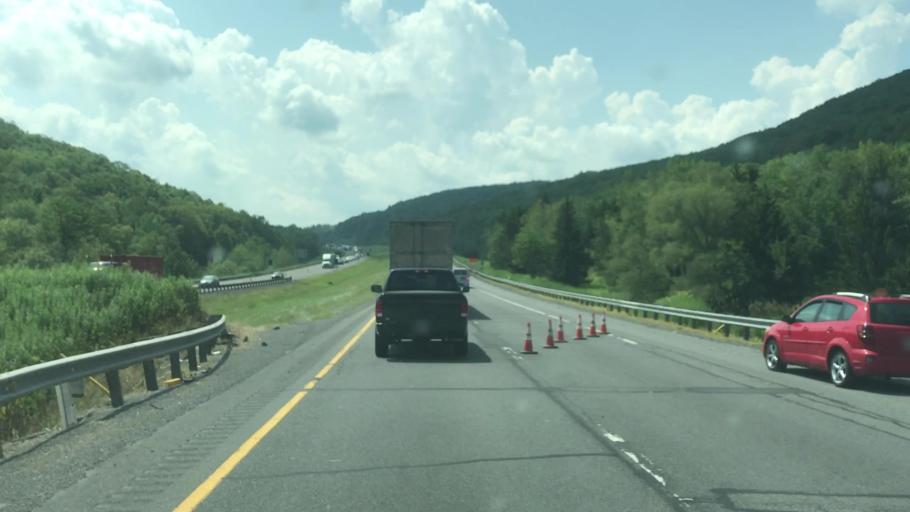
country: US
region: Pennsylvania
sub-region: Lackawanna County
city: Dunmore
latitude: 41.3945
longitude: -75.5837
